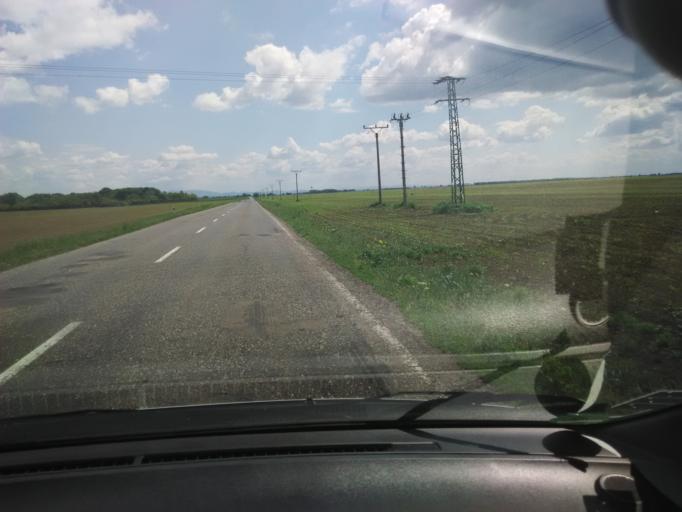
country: SK
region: Nitriansky
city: Levice
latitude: 48.1833
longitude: 18.5226
